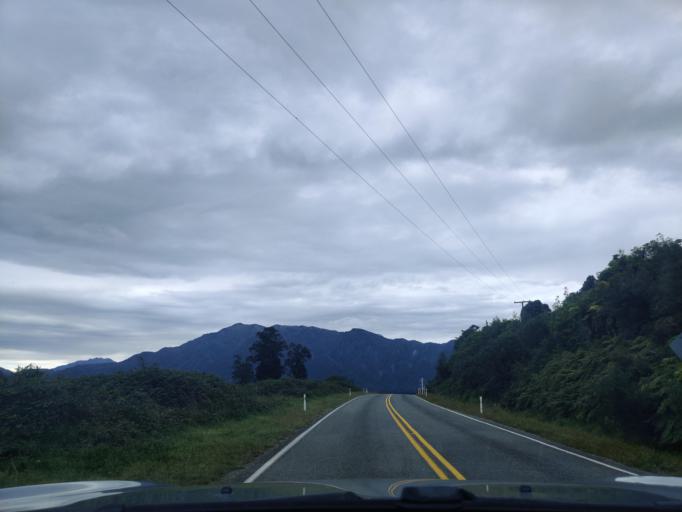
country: NZ
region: West Coast
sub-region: Westland District
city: Hokitika
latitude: -43.1514
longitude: 170.5705
